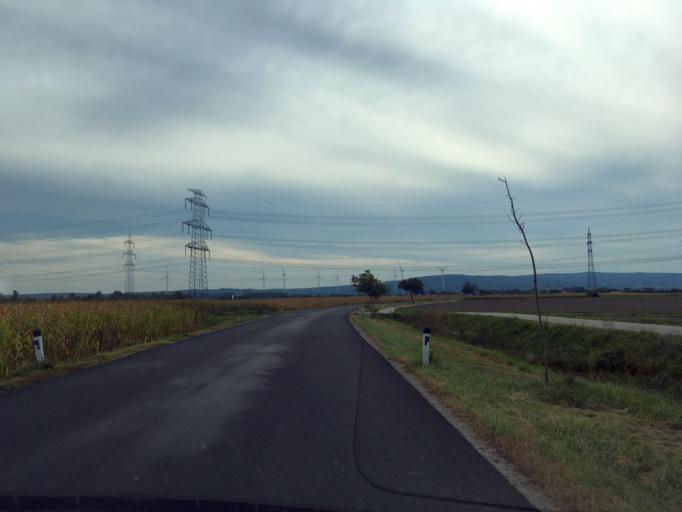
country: AT
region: Lower Austria
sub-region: Politischer Bezirk Bruck an der Leitha
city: Trautmannsdorf an der Leitha
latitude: 48.0331
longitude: 16.6780
